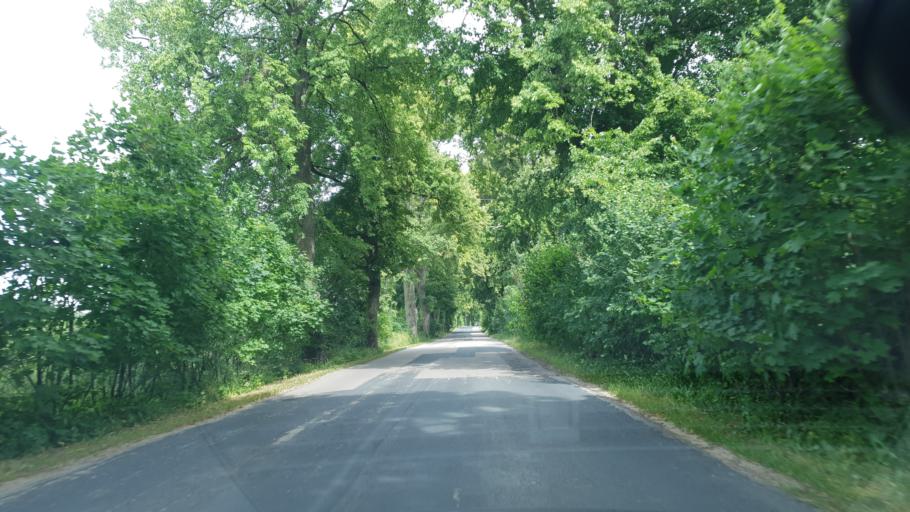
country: PL
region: Pomeranian Voivodeship
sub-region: Powiat kartuski
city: Chmielno
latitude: 54.2682
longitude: 18.0574
